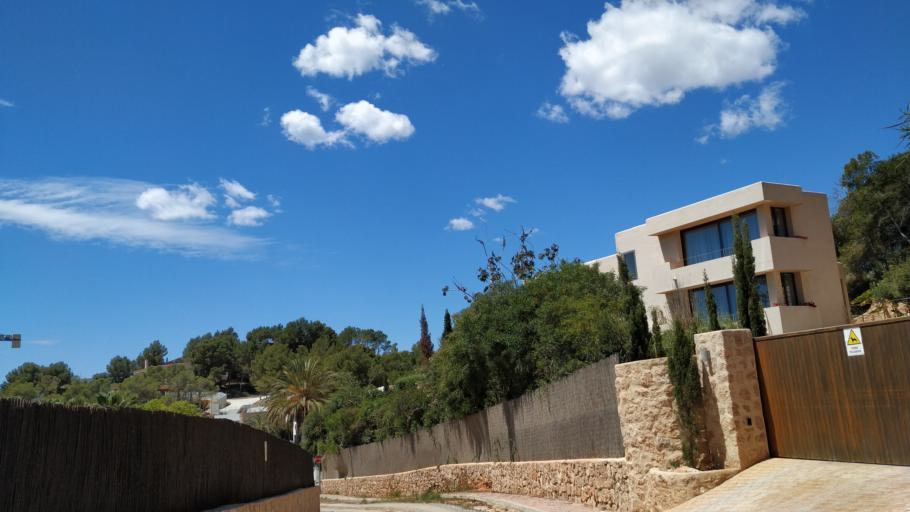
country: ES
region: Balearic Islands
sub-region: Illes Balears
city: Ibiza
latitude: 38.9204
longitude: 1.4735
